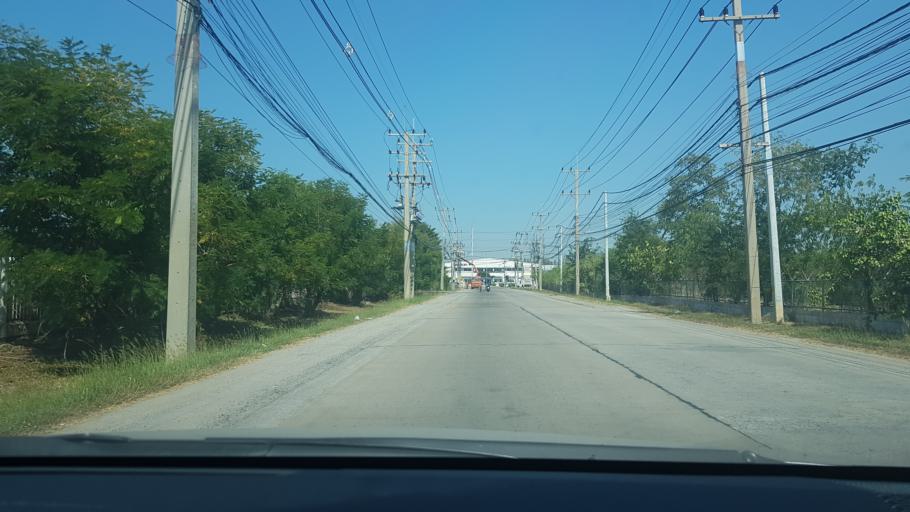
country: TH
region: Phra Nakhon Si Ayutthaya
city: Bang Pa-in
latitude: 14.2503
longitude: 100.6002
